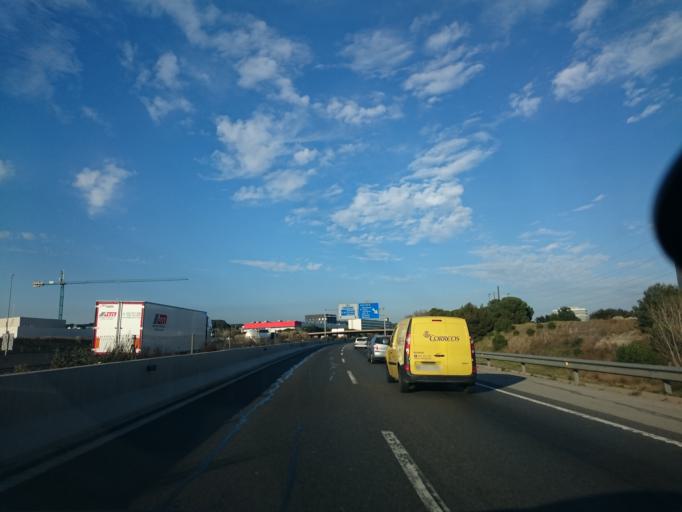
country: ES
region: Catalonia
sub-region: Provincia de Barcelona
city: Rubi
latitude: 41.4837
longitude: 2.0491
